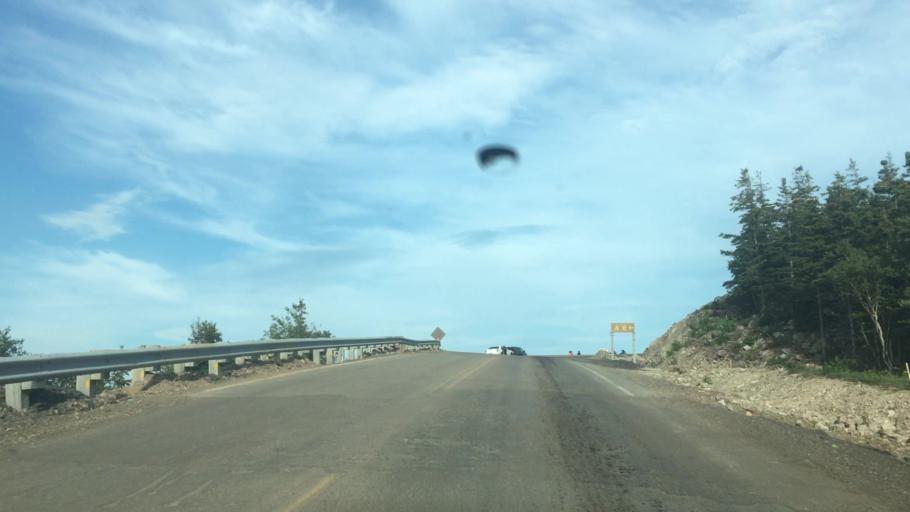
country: CA
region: Nova Scotia
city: Sydney Mines
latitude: 46.8197
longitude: -60.8333
